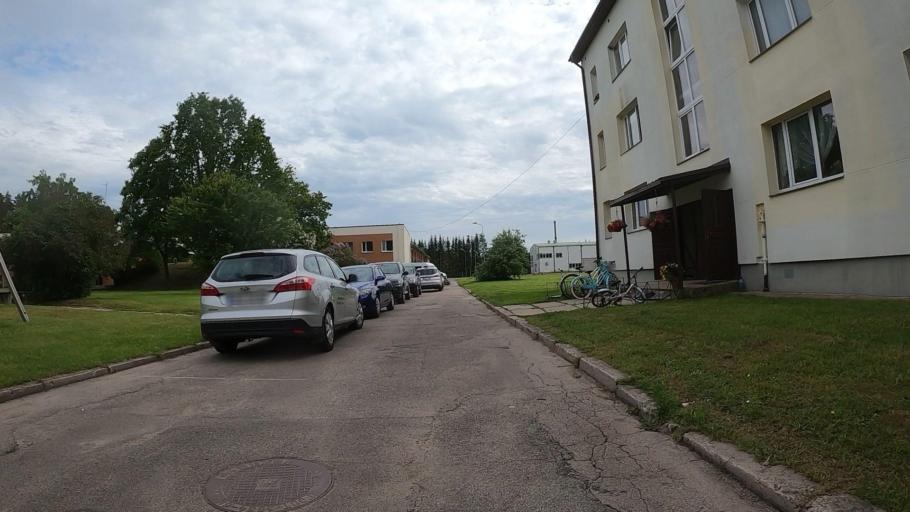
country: LV
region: Ozolnieku
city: Ozolnieki
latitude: 56.6928
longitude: 23.7690
